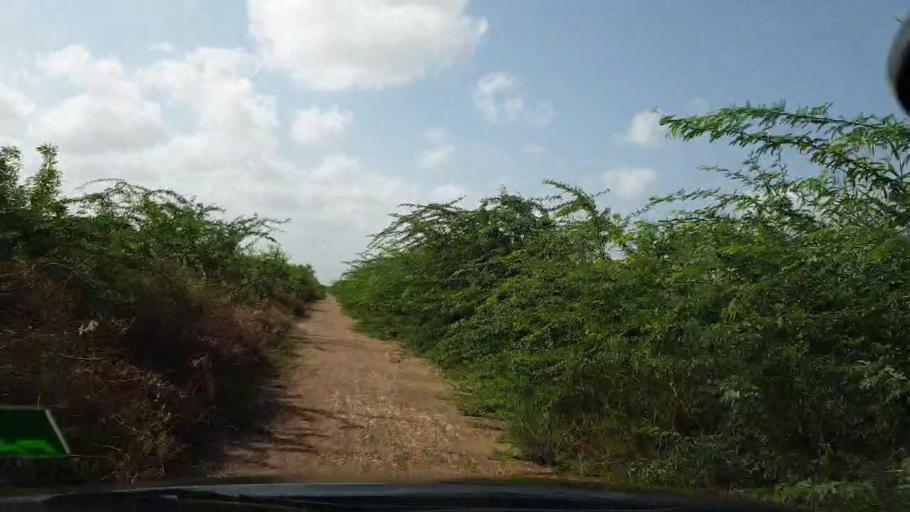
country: PK
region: Sindh
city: Kadhan
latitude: 24.6346
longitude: 69.1049
